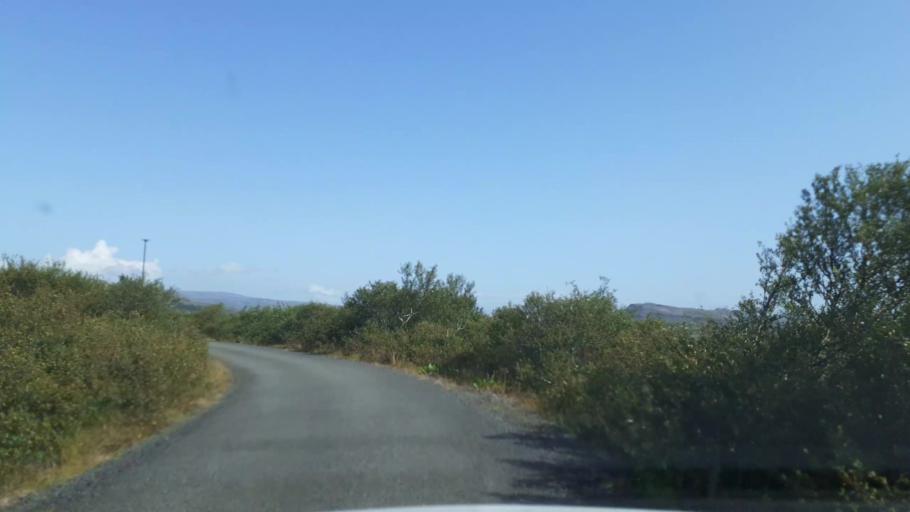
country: IS
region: West
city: Borgarnes
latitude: 64.7016
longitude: -21.6185
